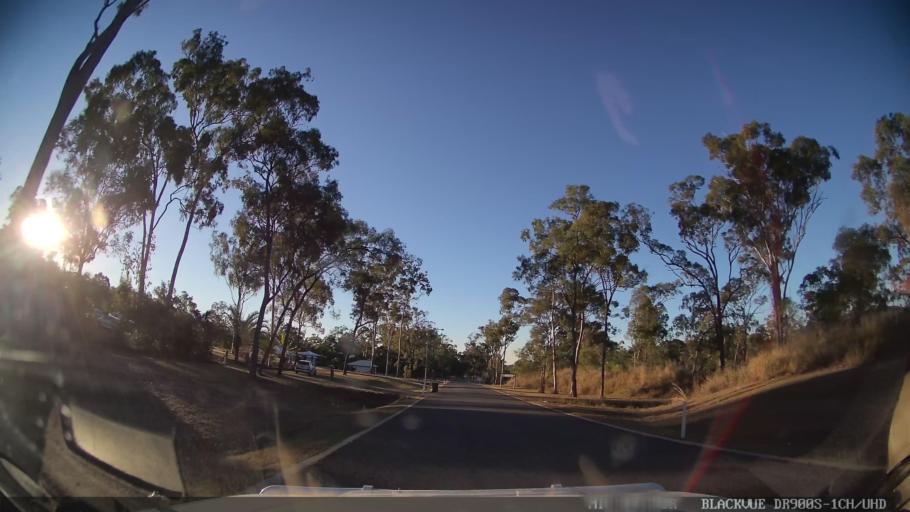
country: AU
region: Queensland
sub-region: Gladstone
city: Toolooa
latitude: -23.9532
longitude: 151.2194
